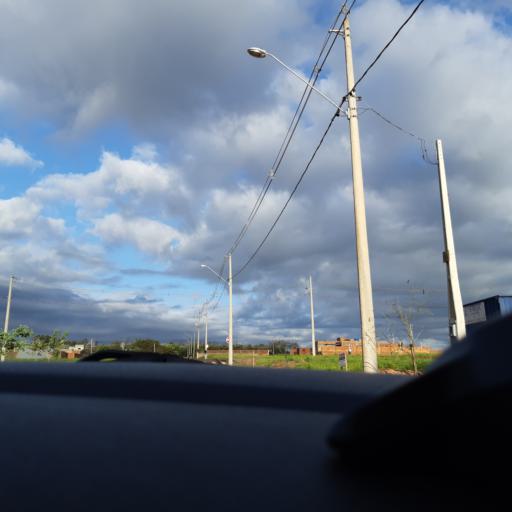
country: BR
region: Sao Paulo
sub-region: Ourinhos
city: Ourinhos
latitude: -23.0038
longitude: -49.8414
